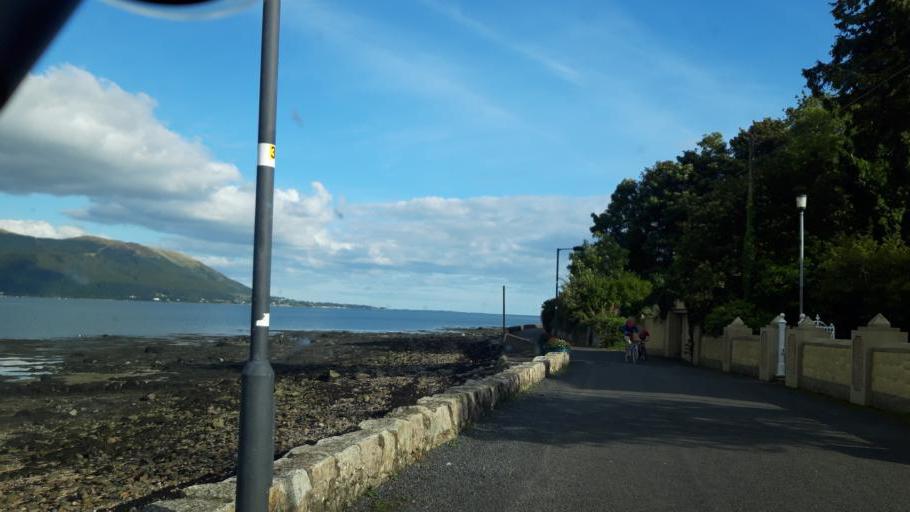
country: GB
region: Northern Ireland
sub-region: Down District
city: Warrenpoint
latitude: 54.0883
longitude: -6.2552
